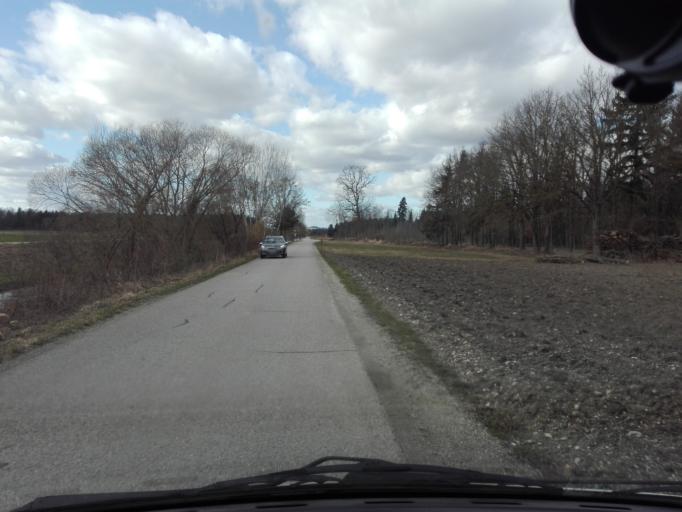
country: AT
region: Upper Austria
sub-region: Politischer Bezirk Perg
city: Perg
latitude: 48.2168
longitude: 14.6720
